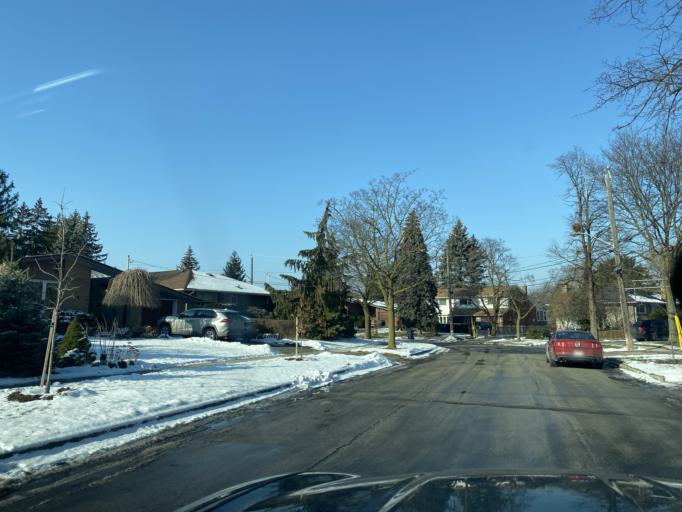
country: CA
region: Ontario
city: Etobicoke
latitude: 43.6615
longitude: -79.5654
